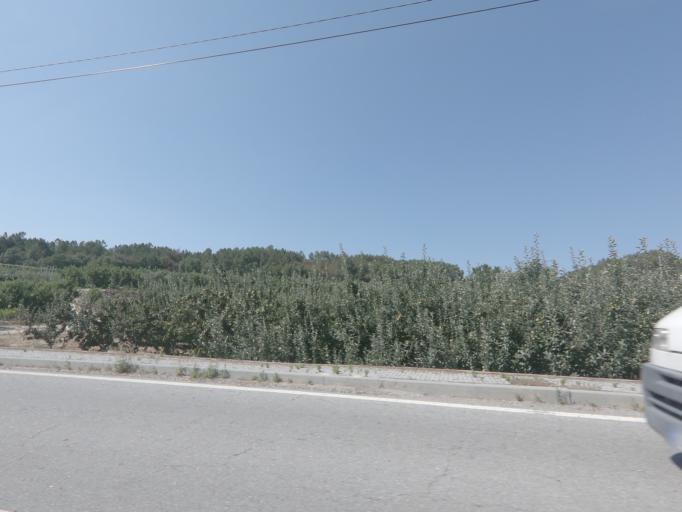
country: PT
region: Viseu
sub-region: Tarouca
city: Tarouca
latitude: 41.0232
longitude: -7.7476
